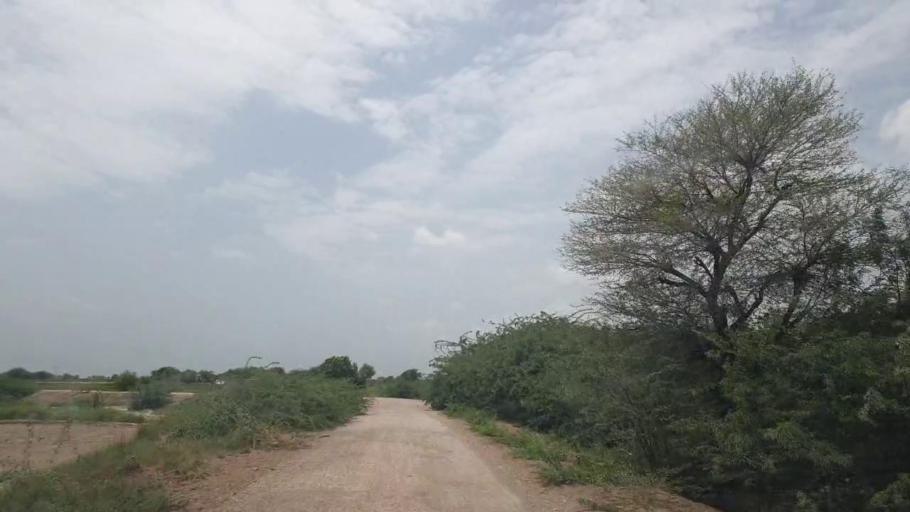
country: PK
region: Sindh
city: Naukot
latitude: 24.9151
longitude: 69.2082
